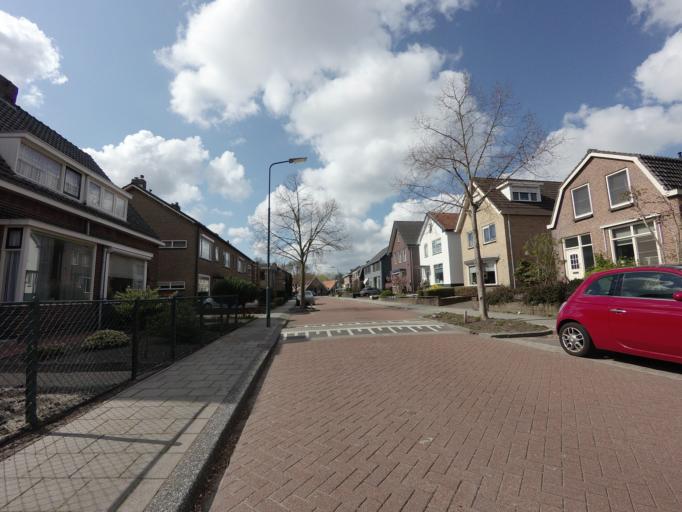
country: NL
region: Utrecht
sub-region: Gemeente Veenendaal
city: Veenendaal
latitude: 52.0346
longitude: 5.5518
